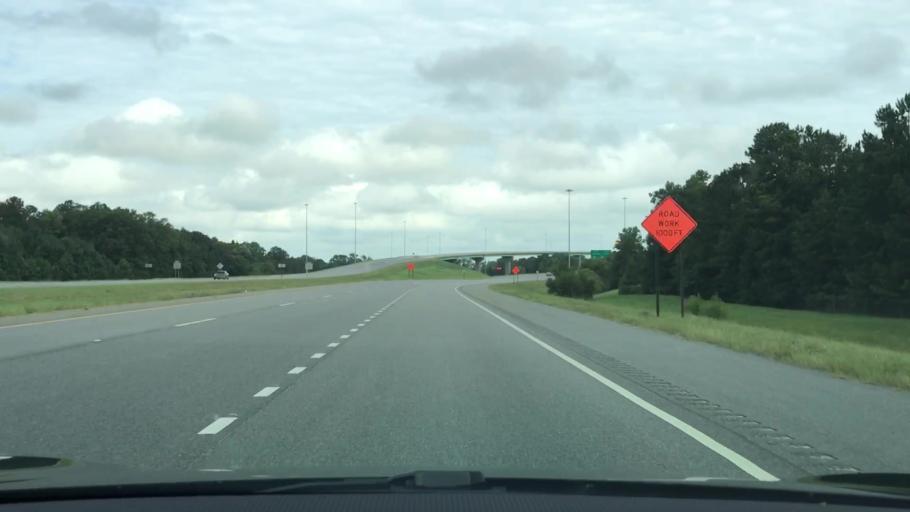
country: US
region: Alabama
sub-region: Montgomery County
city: Pike Road
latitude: 32.3605
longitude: -86.0748
